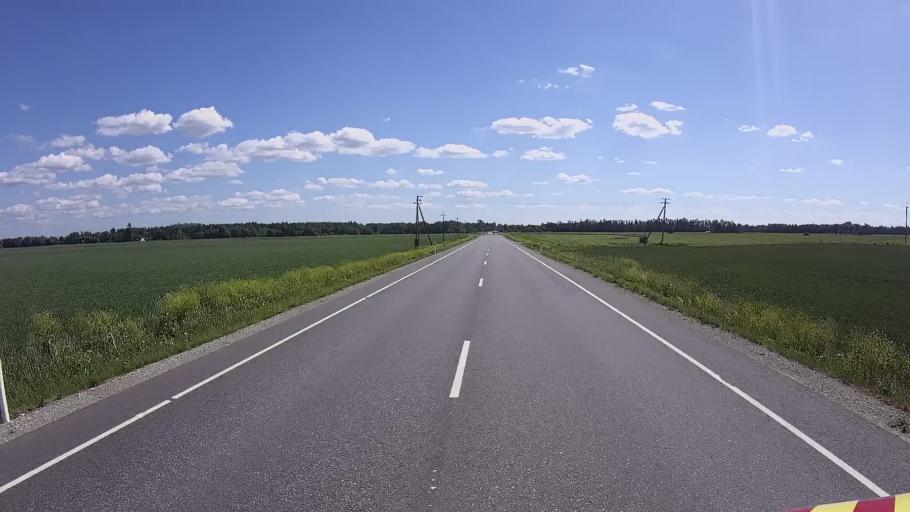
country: EE
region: Ida-Virumaa
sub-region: Johvi vald
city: Johvi
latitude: 59.3652
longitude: 27.3517
